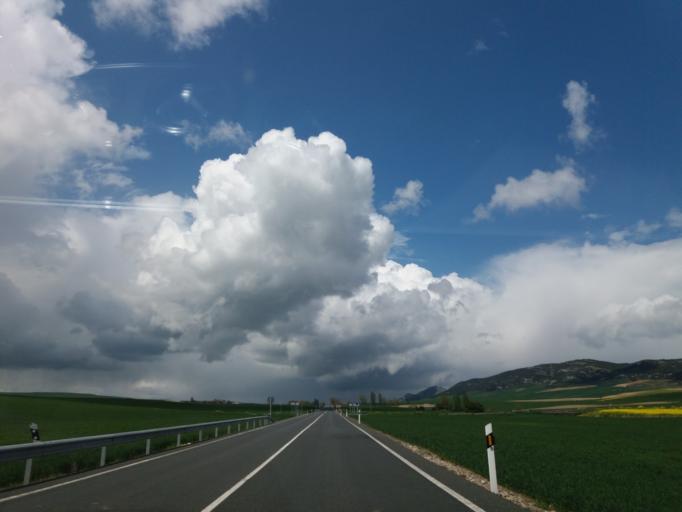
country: ES
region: La Rioja
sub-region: Provincia de La Rioja
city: Foncea
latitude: 42.5964
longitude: -3.0484
